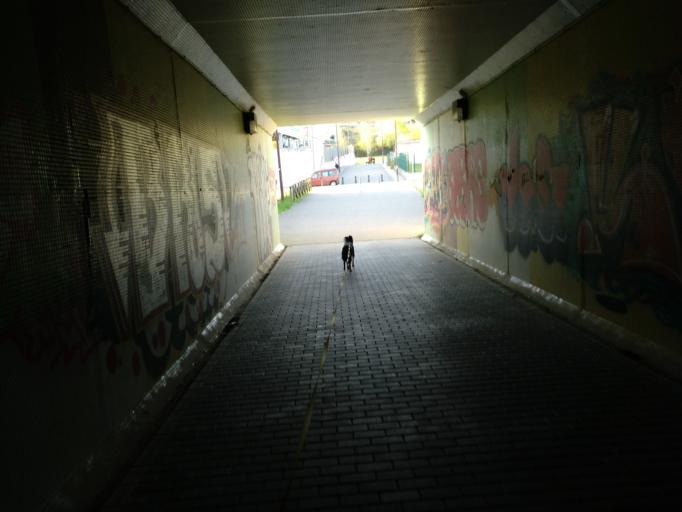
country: ES
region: Asturias
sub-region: Province of Asturias
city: Gijon
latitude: 43.5124
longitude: -5.6634
